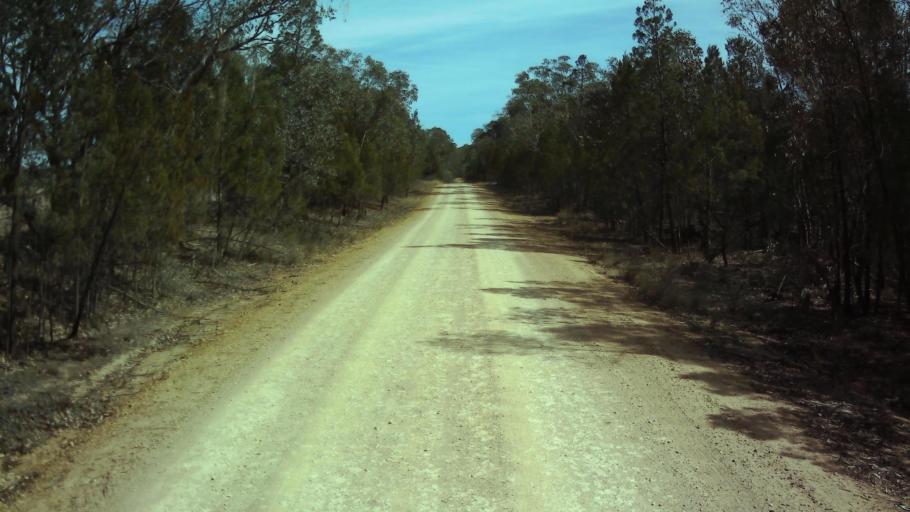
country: AU
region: New South Wales
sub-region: Weddin
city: Grenfell
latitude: -33.8741
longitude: 148.1484
